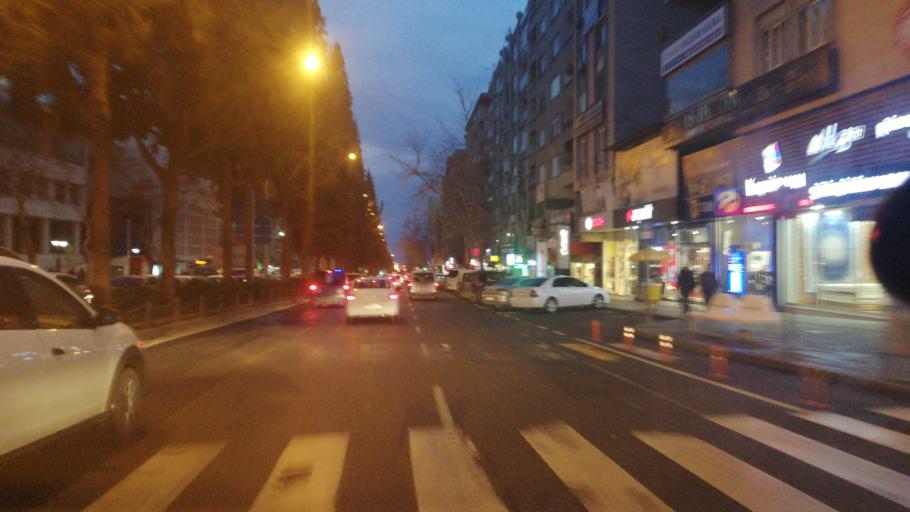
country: TR
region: Kahramanmaras
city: Kahramanmaras
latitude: 37.5777
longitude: 36.9270
